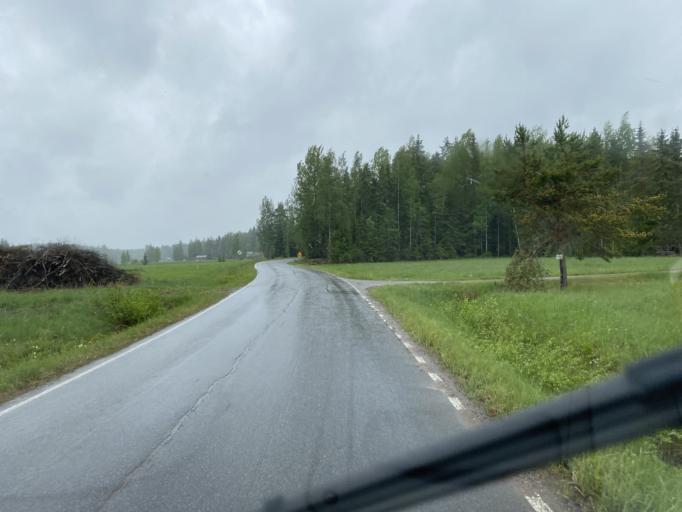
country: FI
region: Haeme
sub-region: Forssa
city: Humppila
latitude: 61.0949
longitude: 23.3166
